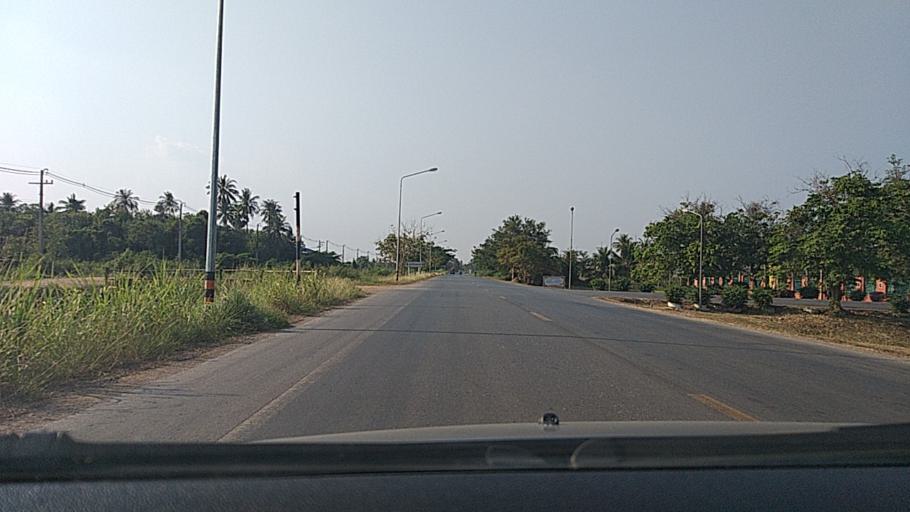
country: TH
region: Sing Buri
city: Phrom Buri
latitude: 14.8170
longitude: 100.4324
